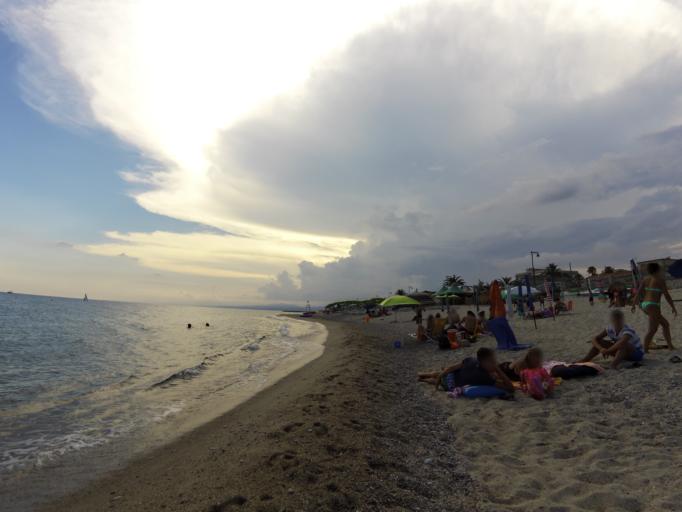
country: IT
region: Calabria
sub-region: Provincia di Reggio Calabria
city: Roccella Ionica
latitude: 38.3197
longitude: 16.4027
